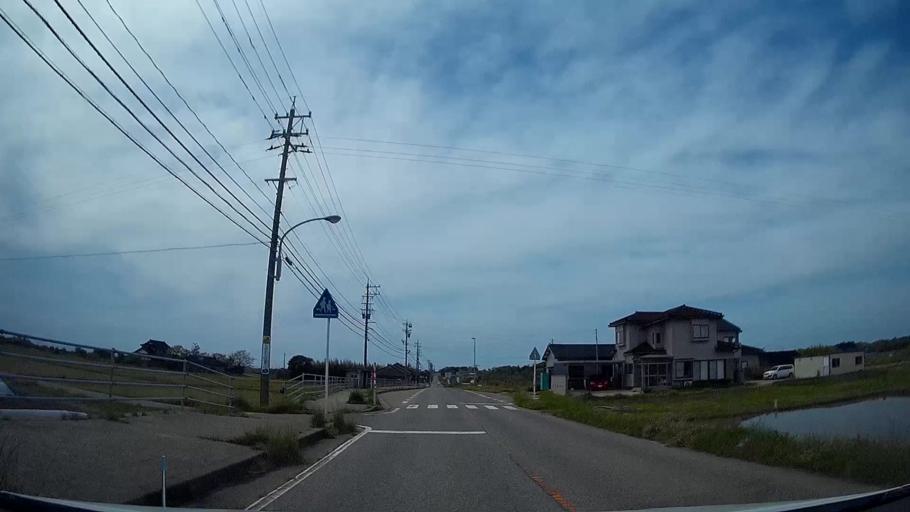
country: JP
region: Ishikawa
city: Hakui
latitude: 37.0115
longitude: 136.7607
